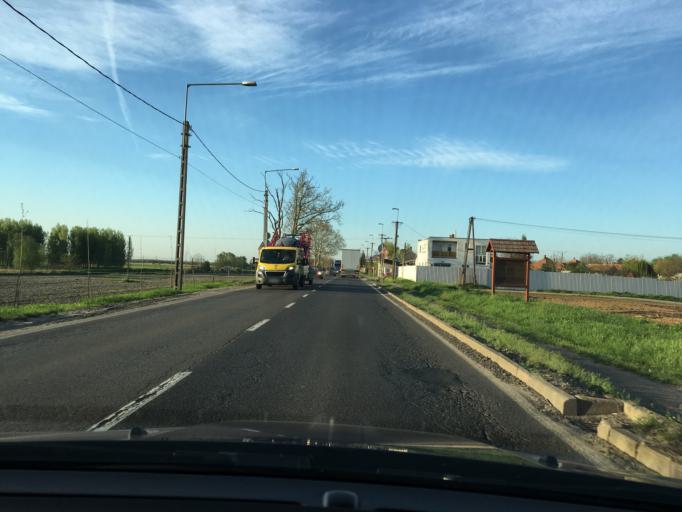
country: HU
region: Hajdu-Bihar
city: Mikepercs
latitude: 47.4335
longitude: 21.6275
